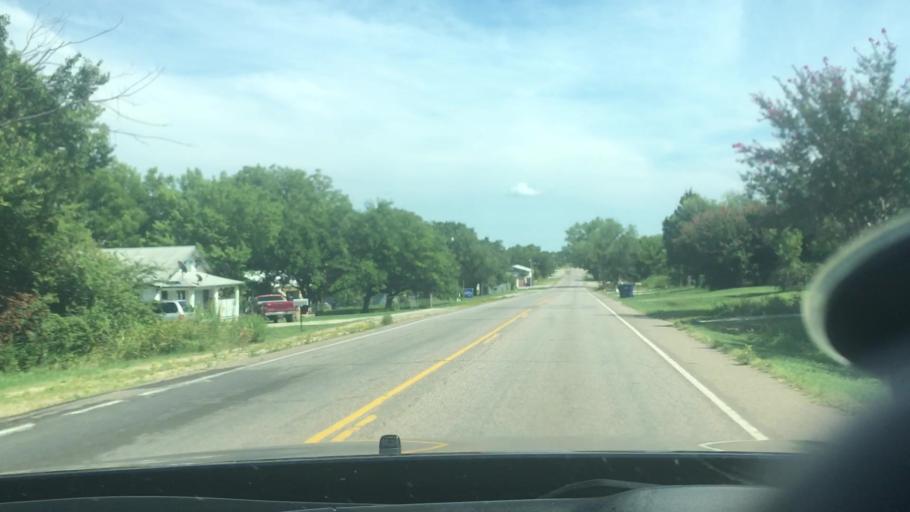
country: US
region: Oklahoma
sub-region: Seminole County
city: Seminole
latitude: 35.2370
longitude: -96.6920
